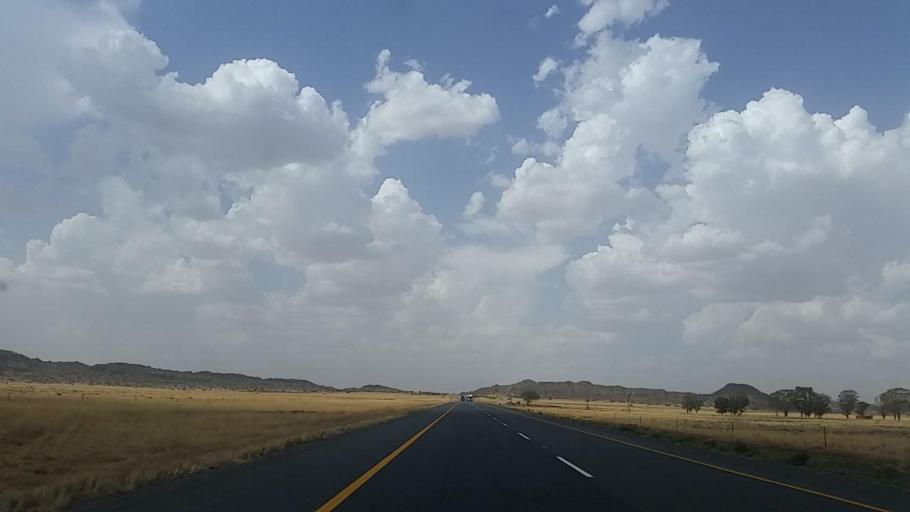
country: ZA
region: Orange Free State
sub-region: Xhariep District Municipality
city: Trompsburg
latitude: -30.4166
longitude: 25.6497
